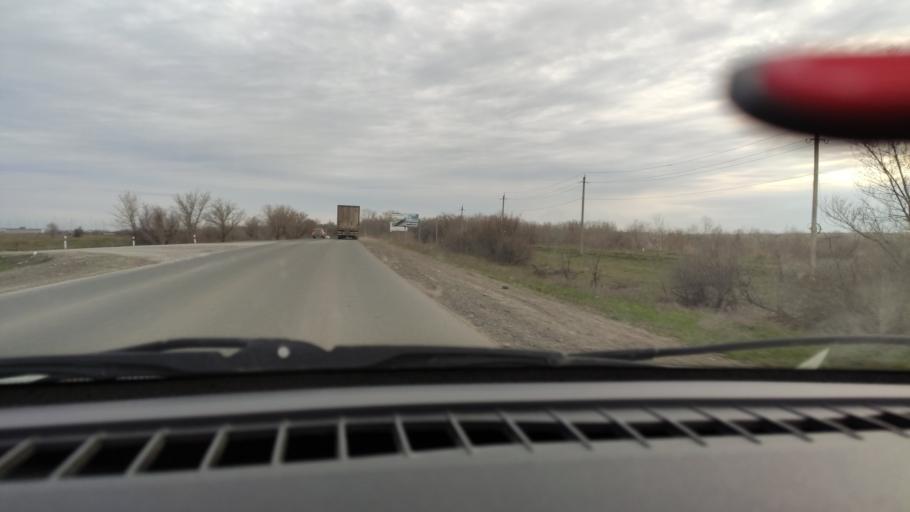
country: RU
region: Orenburg
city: Tatarskaya Kargala
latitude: 51.8973
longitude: 55.1622
